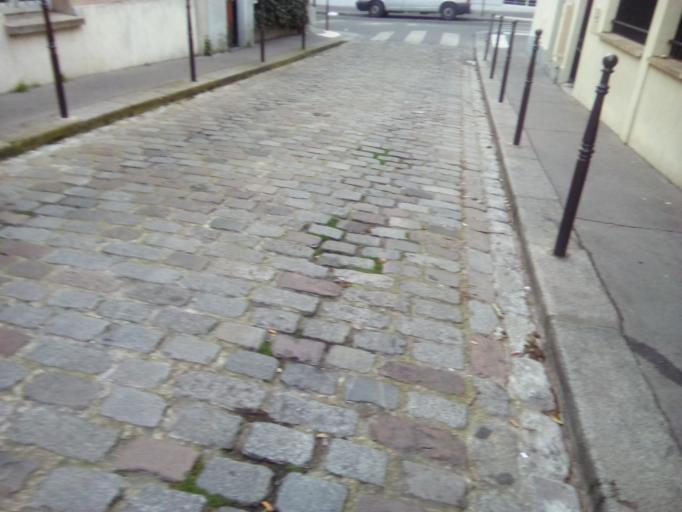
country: FR
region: Ile-de-France
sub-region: Departement de Seine-Saint-Denis
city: Le Pre-Saint-Gervais
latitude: 48.8680
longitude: 2.3928
